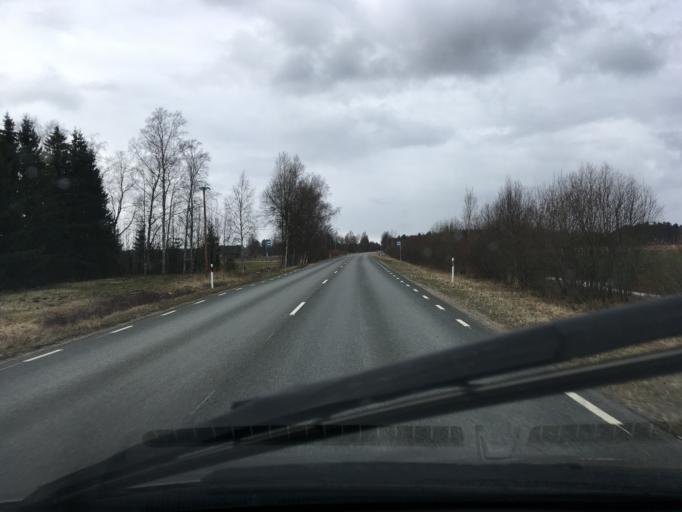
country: EE
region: Laeaene
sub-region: Lihula vald
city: Lihula
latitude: 58.6341
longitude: 23.8667
